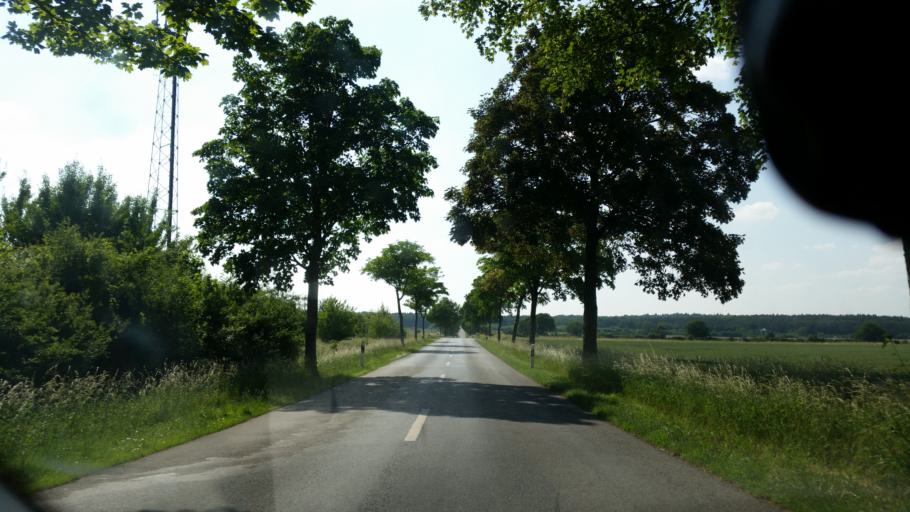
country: DE
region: Lower Saxony
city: Lehre
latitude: 52.3144
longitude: 10.7446
